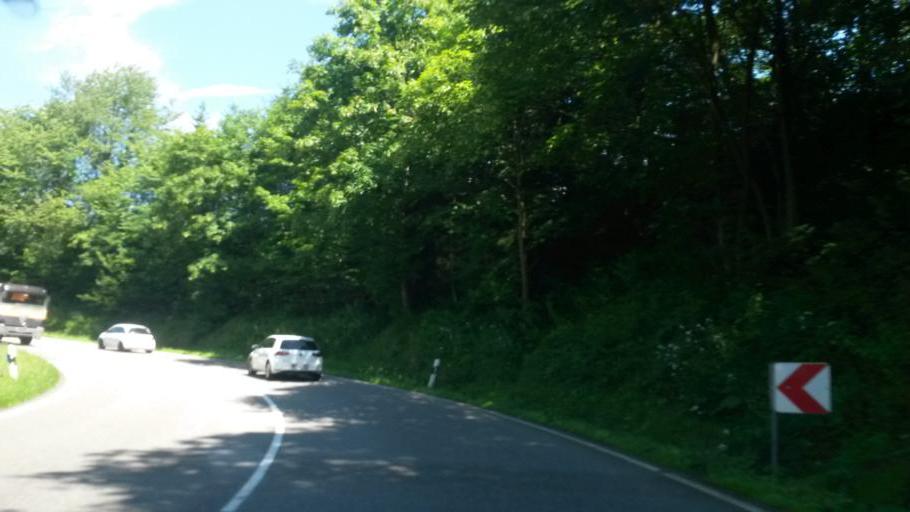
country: DE
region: Baden-Wuerttemberg
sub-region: Karlsruhe Region
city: Pforzheim
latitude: 48.8643
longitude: 8.6931
